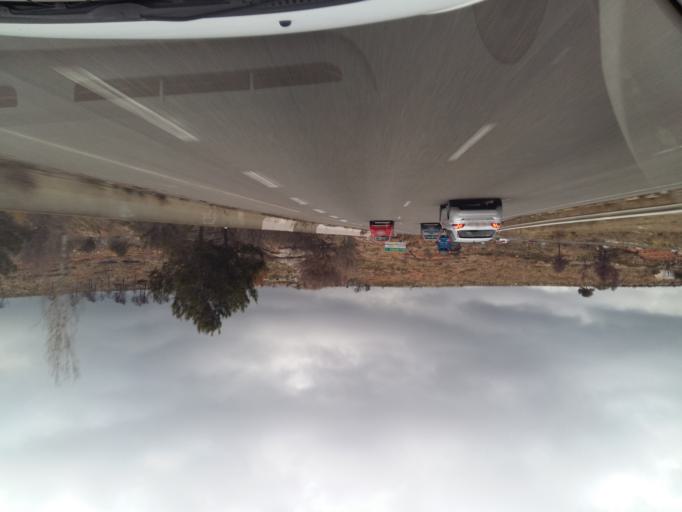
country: FR
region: Provence-Alpes-Cote d'Azur
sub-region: Departement des Bouches-du-Rhone
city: Les Pennes-Mirabeau
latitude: 43.4440
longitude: 5.2979
